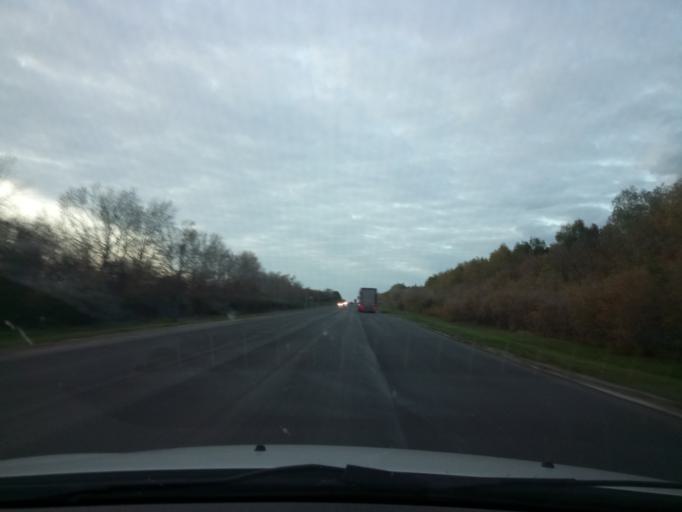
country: RU
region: Nizjnij Novgorod
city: Bol'shoye Murashkino
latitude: 55.8046
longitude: 44.7631
